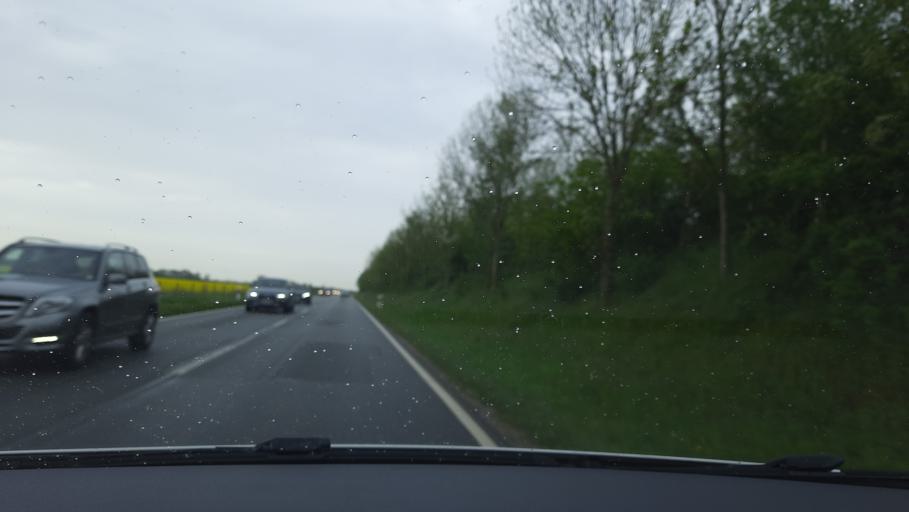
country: DE
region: Lower Saxony
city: Riede
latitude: 53.0061
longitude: 8.8884
